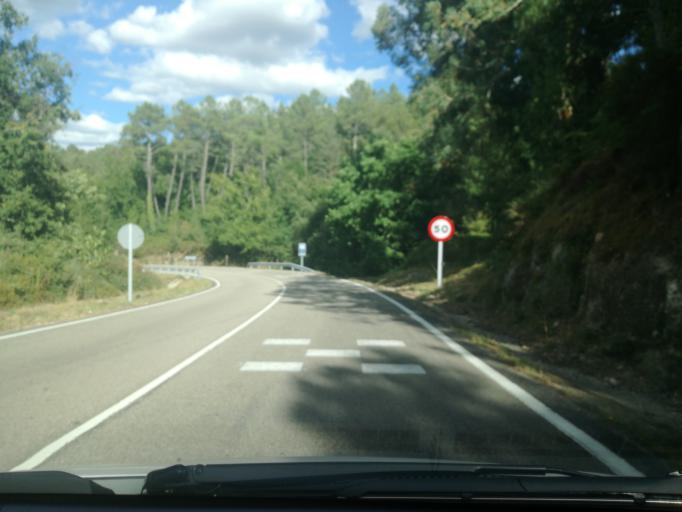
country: ES
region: Galicia
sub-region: Provincia de Ourense
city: Lobios
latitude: 41.8943
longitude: -8.0860
